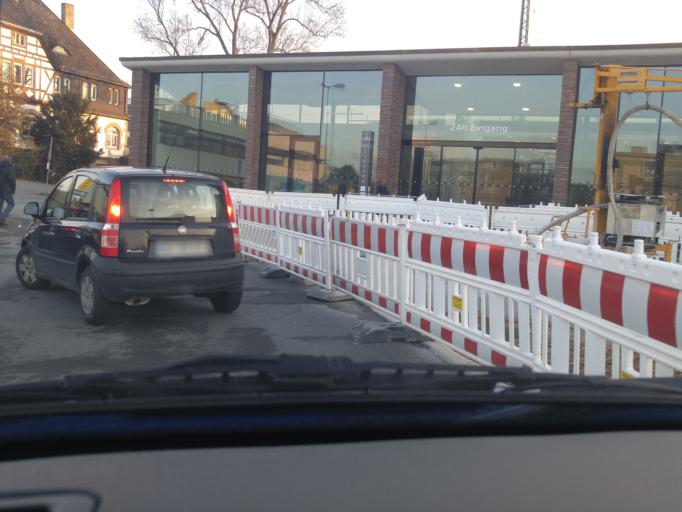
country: DE
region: Hesse
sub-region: Regierungsbezirk Darmstadt
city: Bad Homburg vor der Hoehe
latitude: 50.2206
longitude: 8.6219
